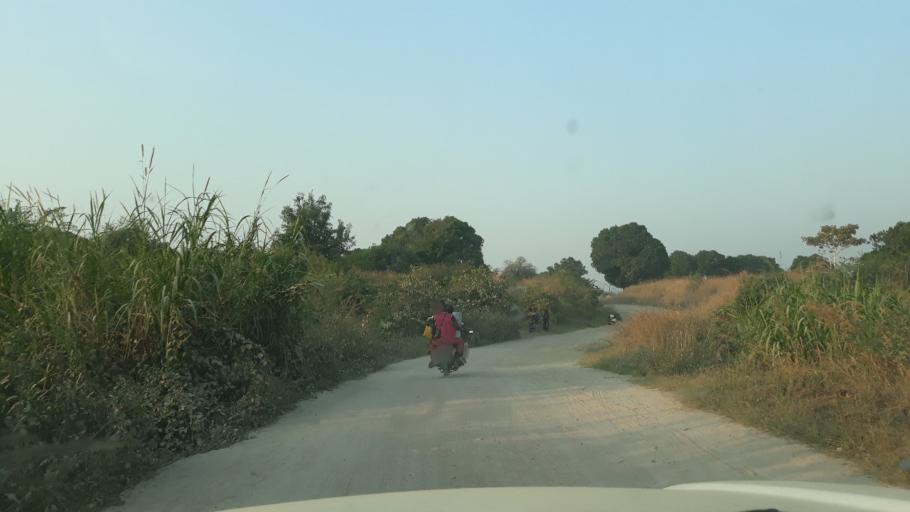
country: BI
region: Bururi
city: Rumonge
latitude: -4.1574
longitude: 29.0696
